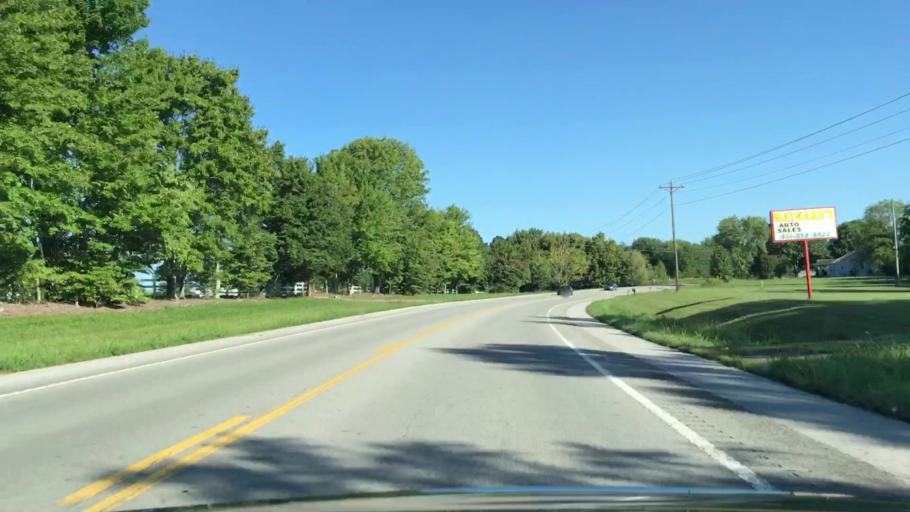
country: US
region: Tennessee
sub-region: Jackson County
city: Dodson Branch
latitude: 36.2691
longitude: -85.6170
